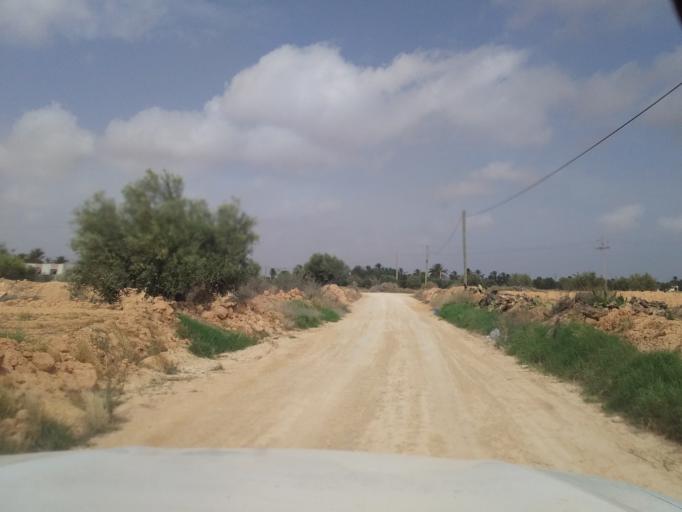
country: TN
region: Qabis
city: Gabes
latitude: 33.6298
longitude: 10.3067
